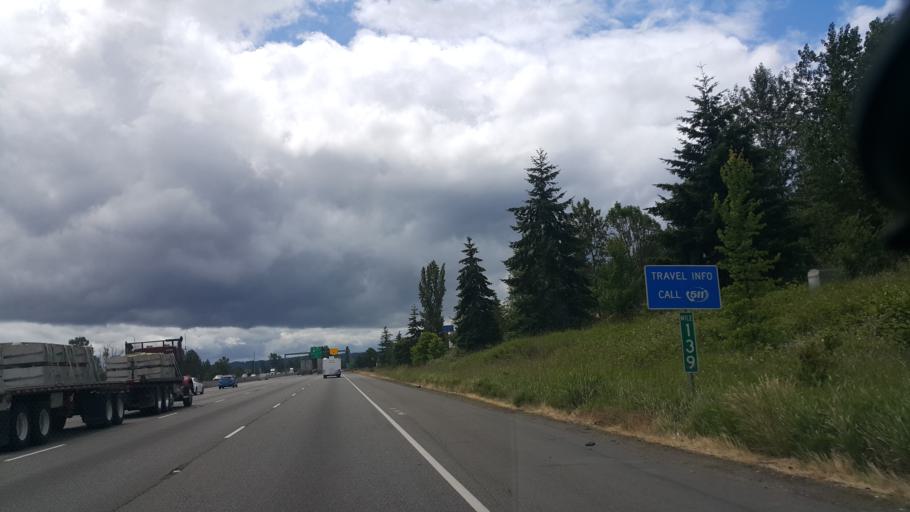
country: US
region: Washington
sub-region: Pierce County
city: Fife Heights
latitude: 47.2509
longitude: -122.3331
